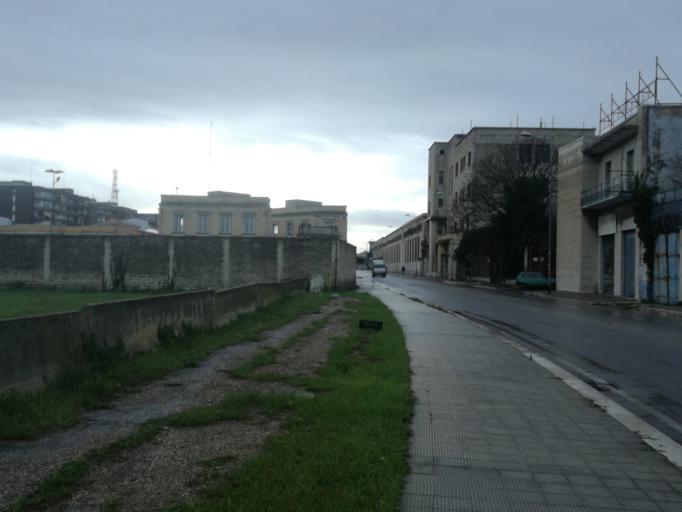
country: IT
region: Apulia
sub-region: Provincia di Bari
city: Bari
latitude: 41.1308
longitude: 16.8443
